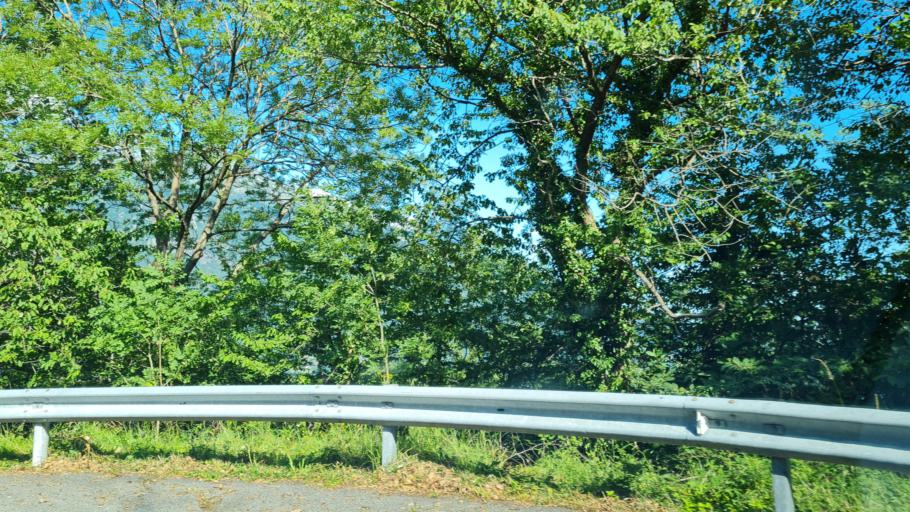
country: IT
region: Piedmont
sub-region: Provincia di Torino
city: Quincinetto
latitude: 45.5556
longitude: 7.7961
